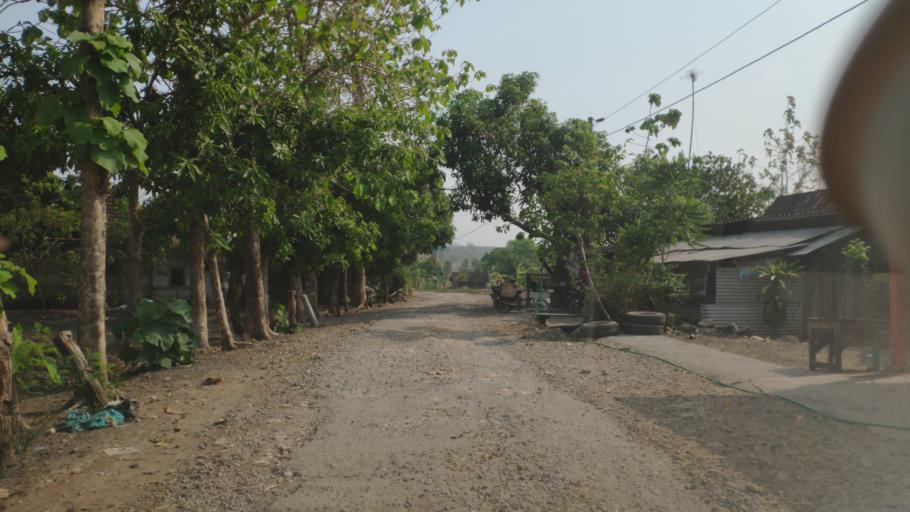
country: ID
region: Central Java
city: Randublatung
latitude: -7.2804
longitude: 111.2658
